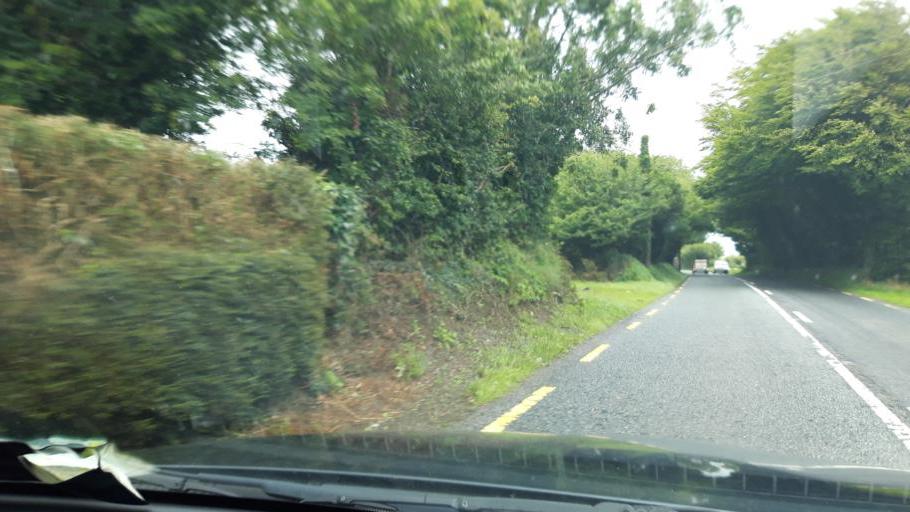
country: IE
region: Leinster
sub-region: Loch Garman
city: New Ross
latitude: 52.4333
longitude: -6.7610
